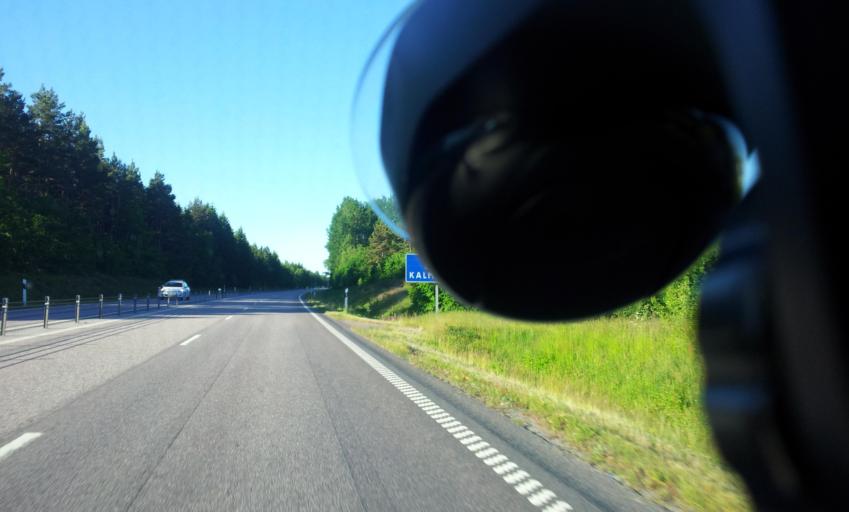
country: SE
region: Kalmar
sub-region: Monsteras Kommun
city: Moensteras
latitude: 57.0208
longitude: 16.4290
